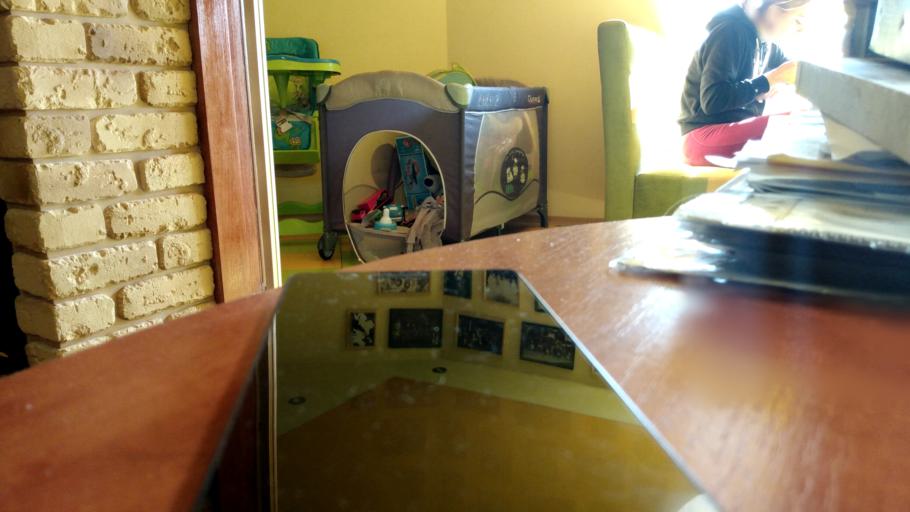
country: RU
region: Penza
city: Serdobsk
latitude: 52.4281
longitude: 44.3078
